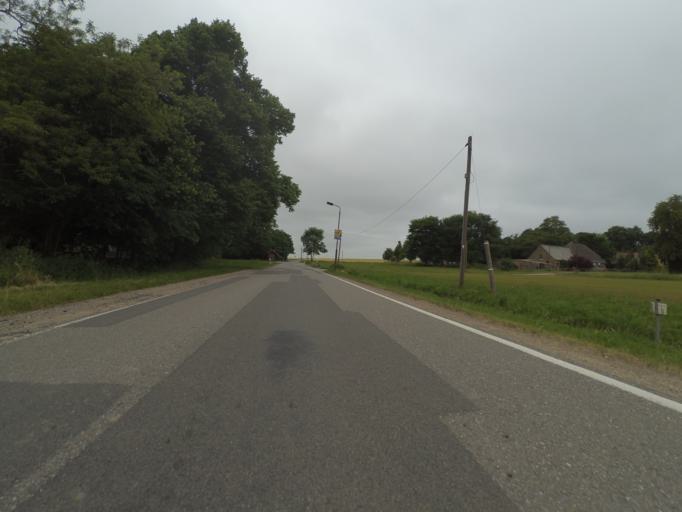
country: DE
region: Mecklenburg-Vorpommern
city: Gaegelow
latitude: 53.6853
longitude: 11.8969
